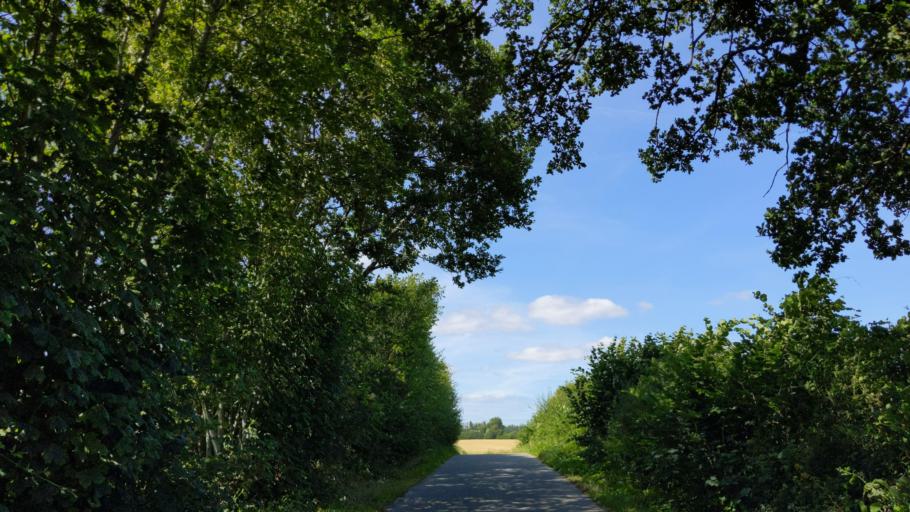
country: DE
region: Schleswig-Holstein
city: Kasseedorf
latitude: 54.1341
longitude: 10.7381
